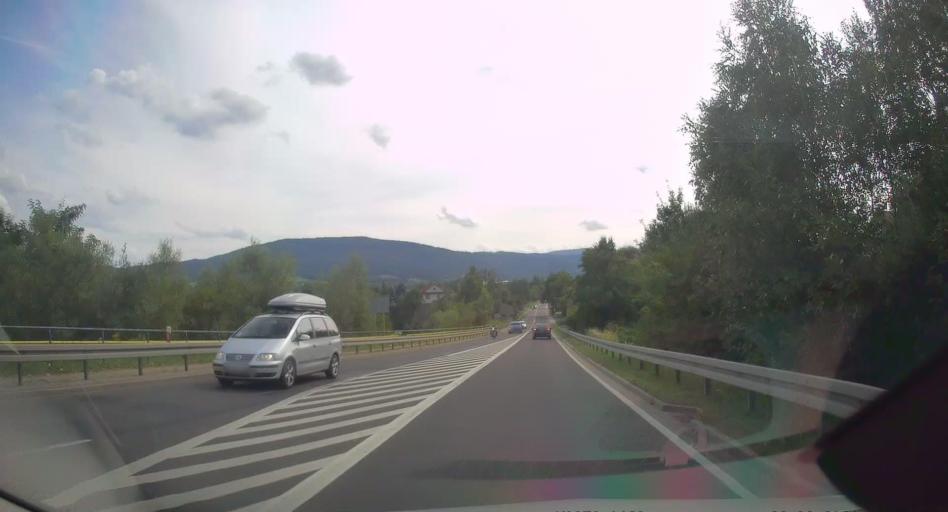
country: PL
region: Lesser Poland Voivodeship
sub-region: Powiat myslenicki
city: Borzeta
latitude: 49.8510
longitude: 19.9686
